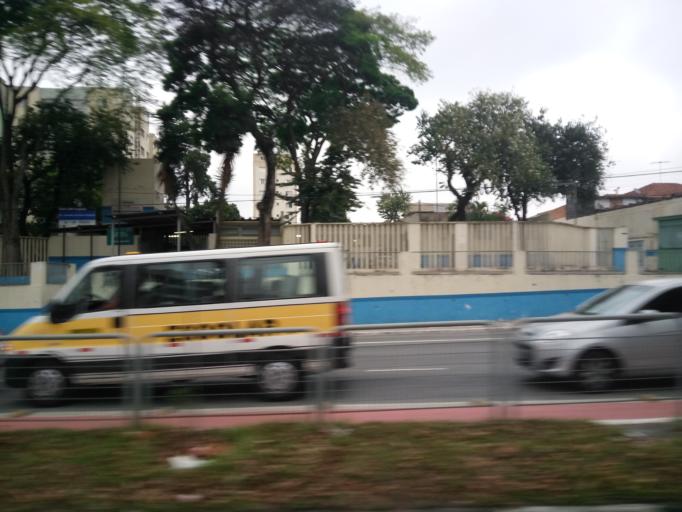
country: BR
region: Sao Paulo
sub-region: Diadema
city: Diadema
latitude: -23.6518
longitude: -46.6378
